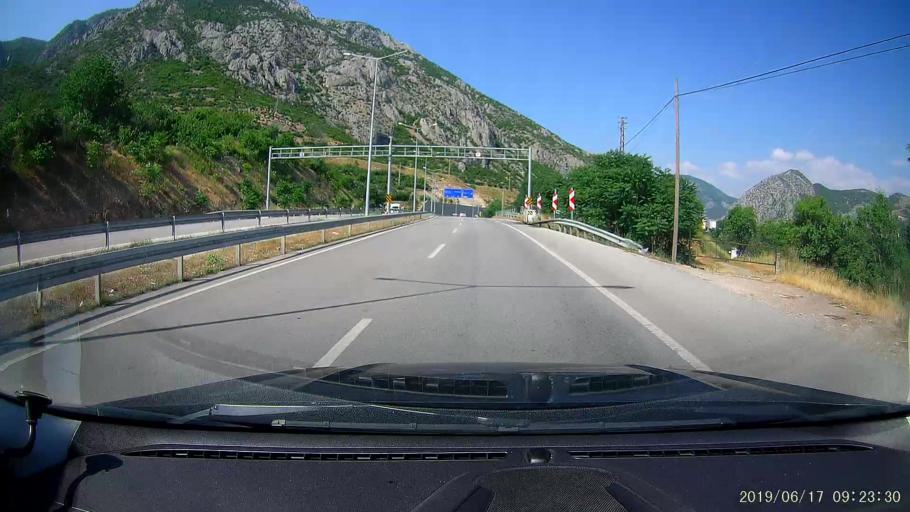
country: TR
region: Amasya
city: Amasya
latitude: 40.6755
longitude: 35.8728
